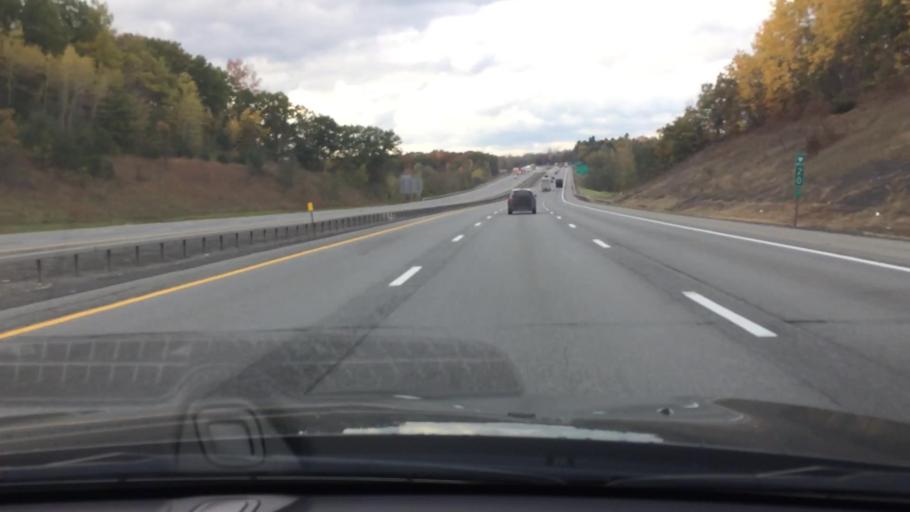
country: US
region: New York
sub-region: Saratoga County
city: Country Knolls
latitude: 42.9565
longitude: -73.8023
